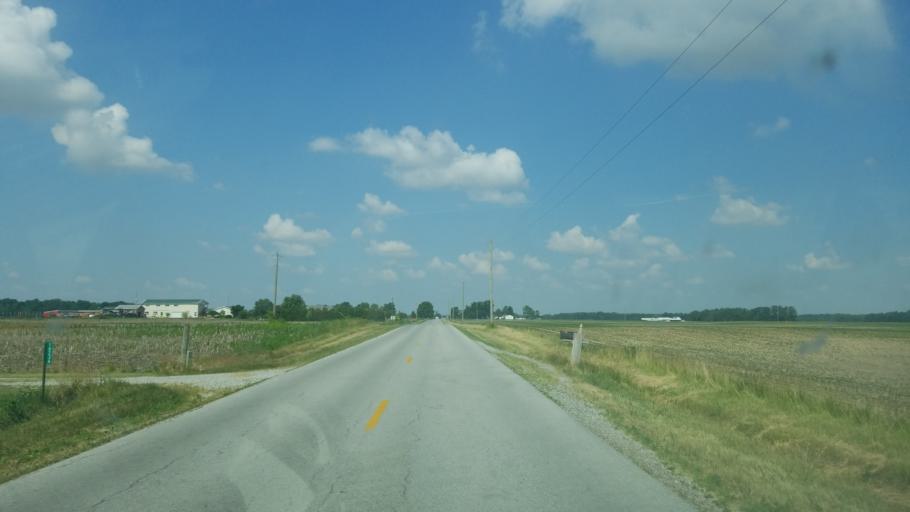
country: US
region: Ohio
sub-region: Auglaize County
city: Wapakoneta
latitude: 40.5703
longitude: -84.1410
